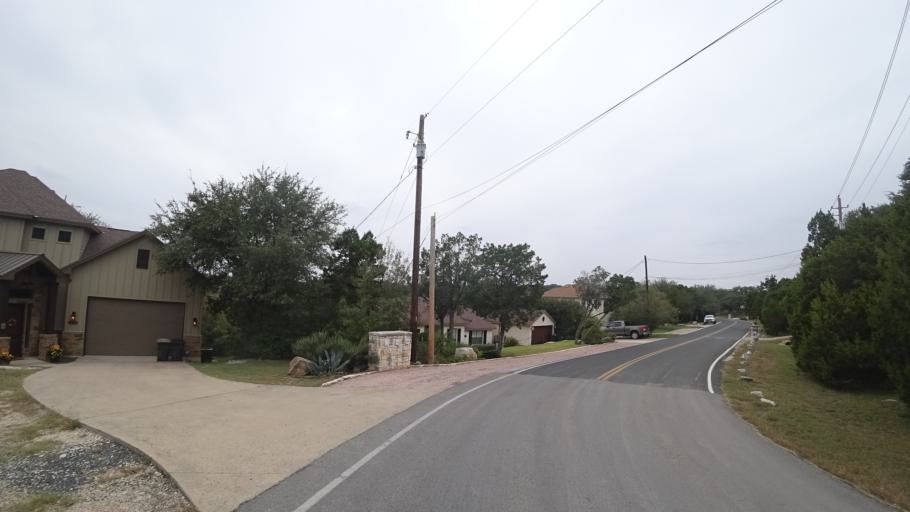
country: US
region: Texas
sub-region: Travis County
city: Hudson Bend
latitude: 30.3683
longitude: -97.9269
